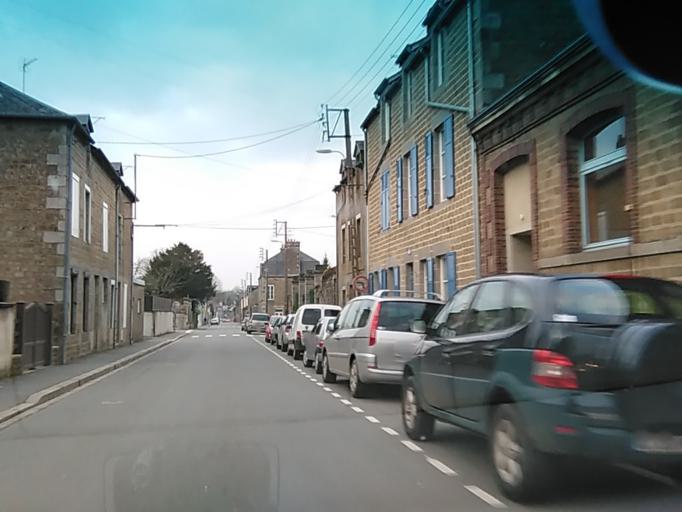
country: FR
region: Lower Normandy
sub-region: Departement de l'Orne
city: La Ferte-Mace
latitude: 48.5909
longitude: -0.3549
